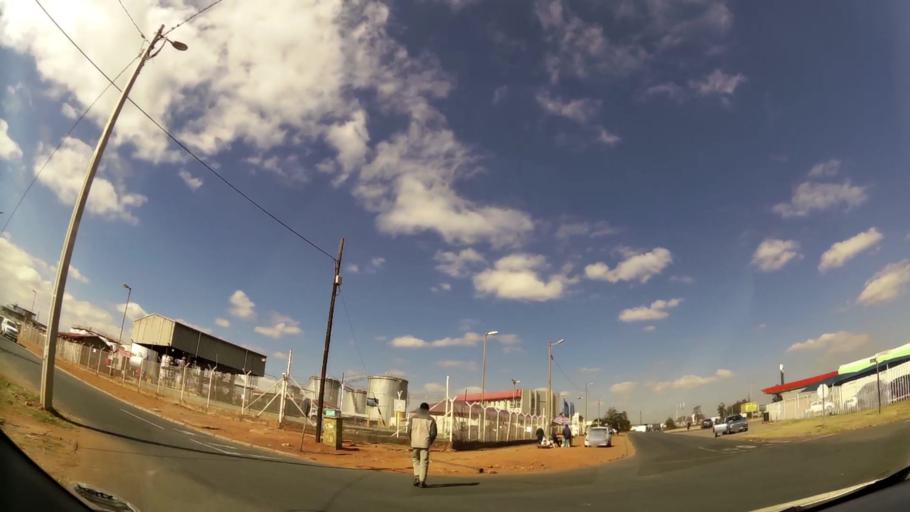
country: ZA
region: Gauteng
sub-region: West Rand District Municipality
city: Krugersdorp
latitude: -26.1179
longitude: 27.8107
